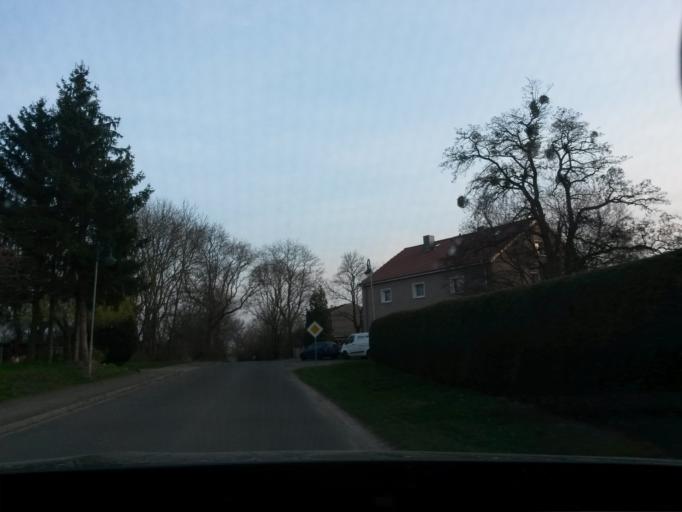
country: DE
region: Brandenburg
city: Protzel
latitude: 52.5881
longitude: 13.9507
